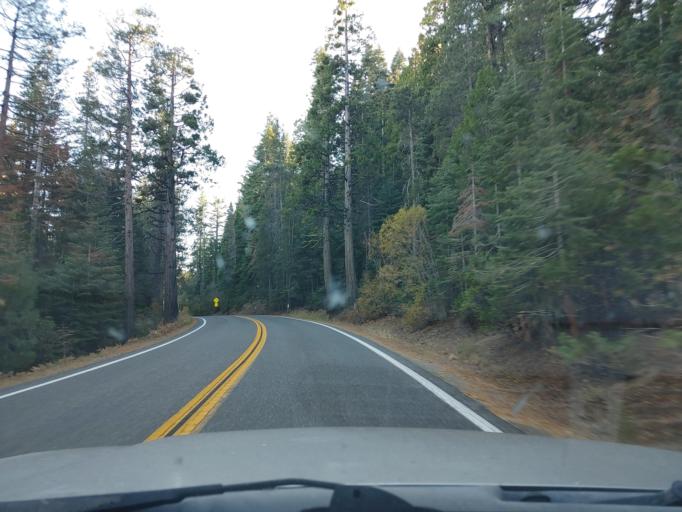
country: US
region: California
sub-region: Placer County
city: Tahoma
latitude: 38.9982
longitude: -120.1107
